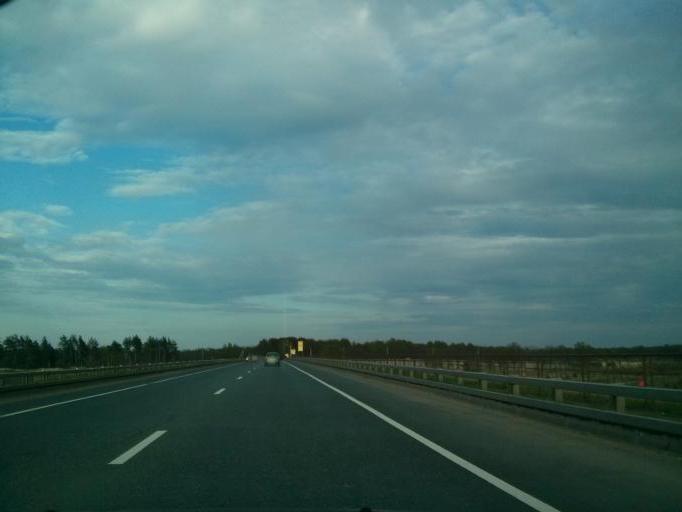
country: RU
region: Nizjnij Novgorod
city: Navashino
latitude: 55.5867
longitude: 42.1431
